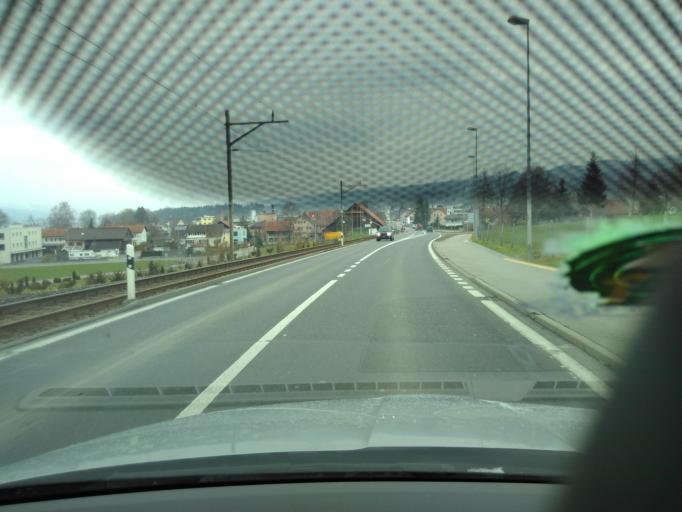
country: CH
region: Lucerne
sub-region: Hochdorf District
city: Hochdorf
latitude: 47.1812
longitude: 8.2807
